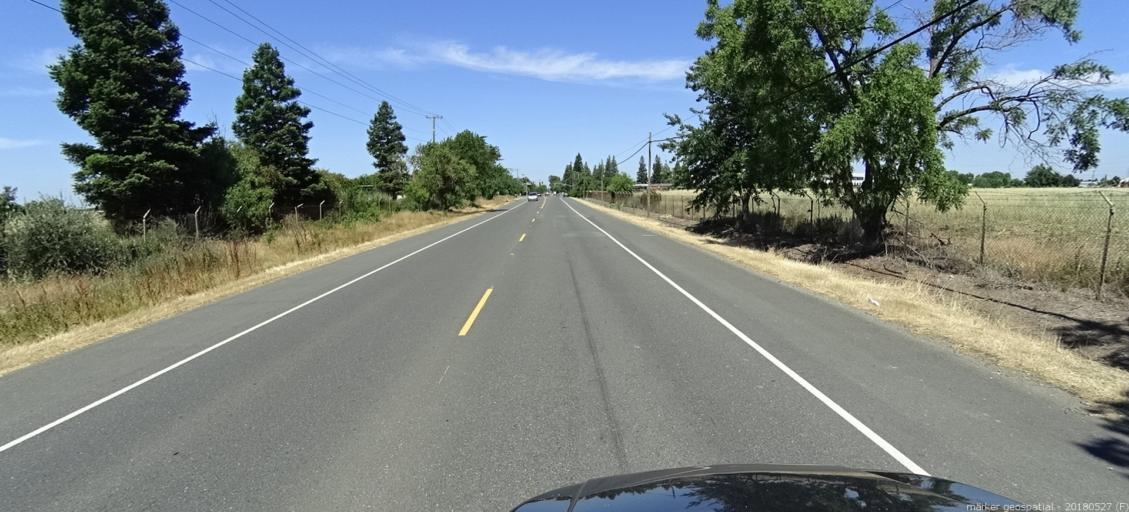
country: US
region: California
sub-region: Sacramento County
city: Rosemont
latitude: 38.5434
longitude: -121.3874
